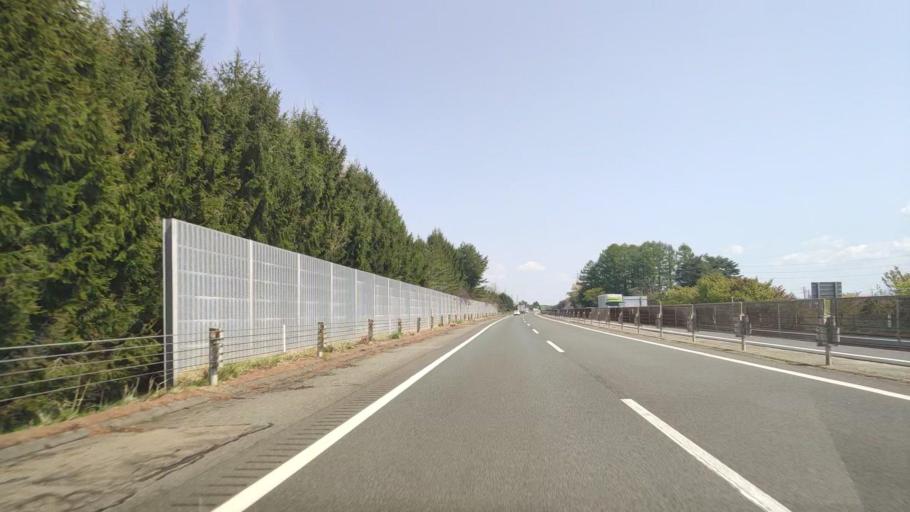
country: JP
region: Iwate
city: Morioka-shi
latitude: 39.7638
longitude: 141.1001
